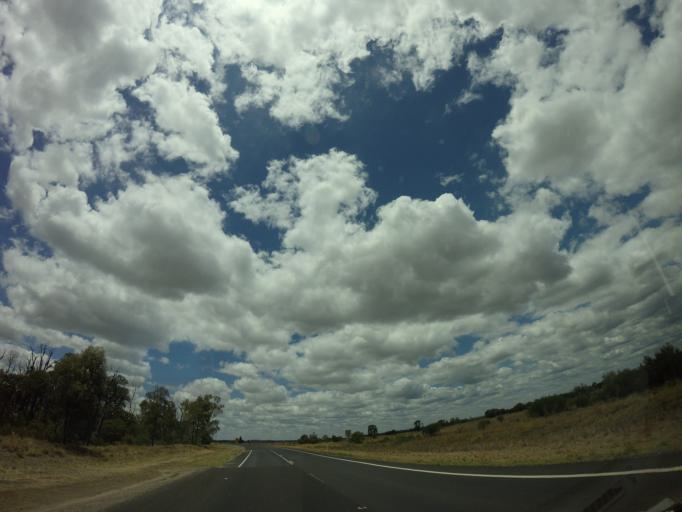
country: AU
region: Queensland
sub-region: Goondiwindi
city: Goondiwindi
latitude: -28.1543
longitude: 150.6761
